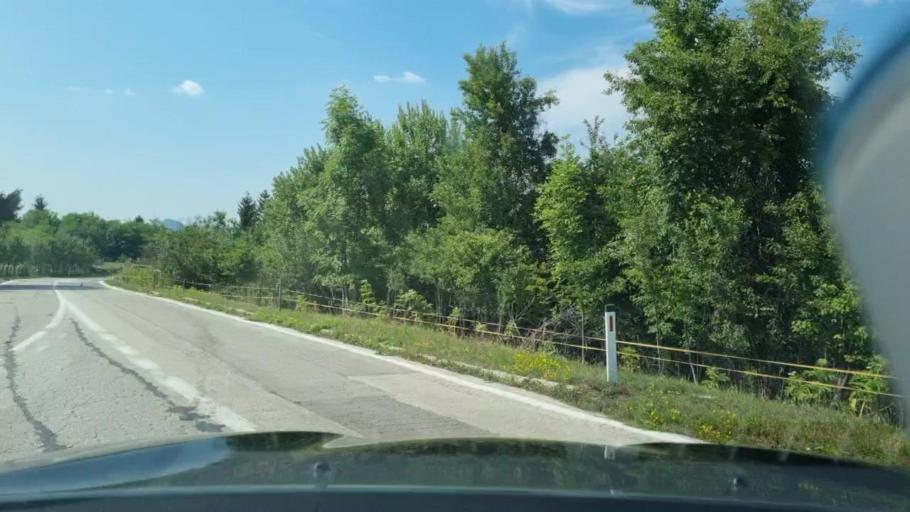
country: BA
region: Federation of Bosnia and Herzegovina
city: Bosanska Krupa
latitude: 44.8283
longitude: 16.1774
